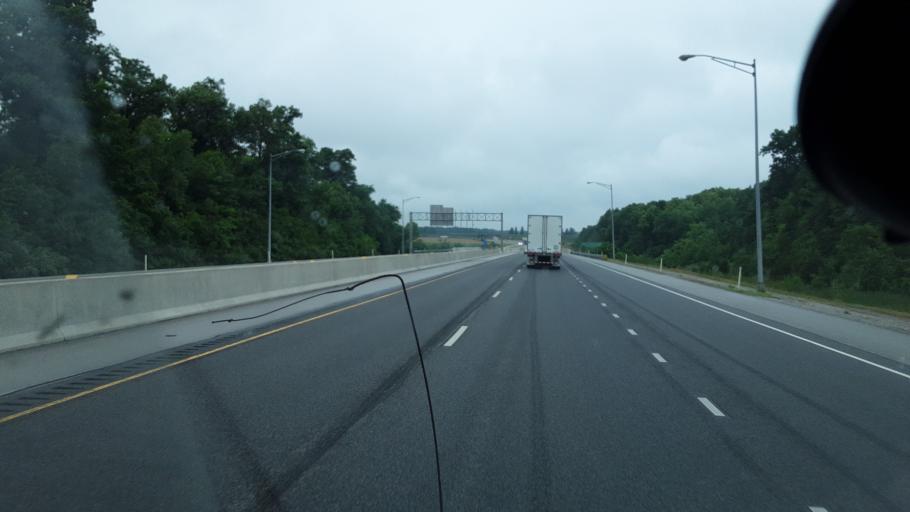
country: US
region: Indiana
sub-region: Allen County
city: New Haven
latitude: 40.9824
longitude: -85.0917
